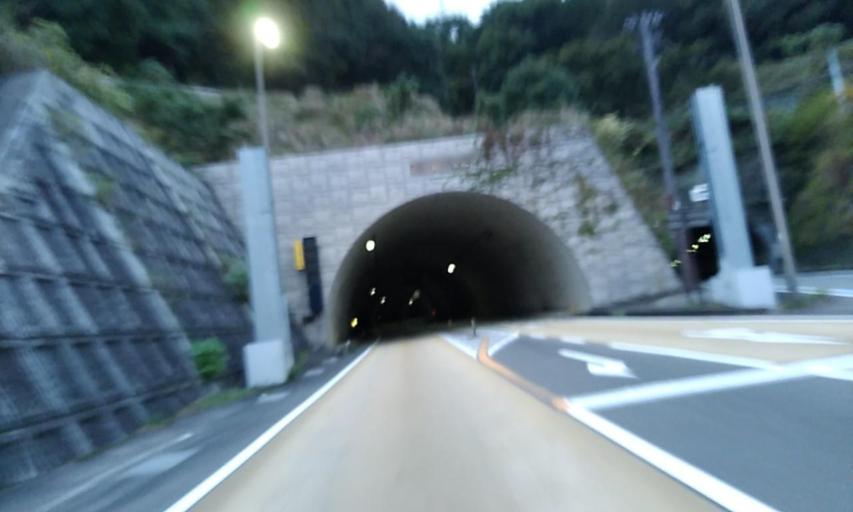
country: JP
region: Wakayama
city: Shingu
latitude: 33.7194
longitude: 135.9795
